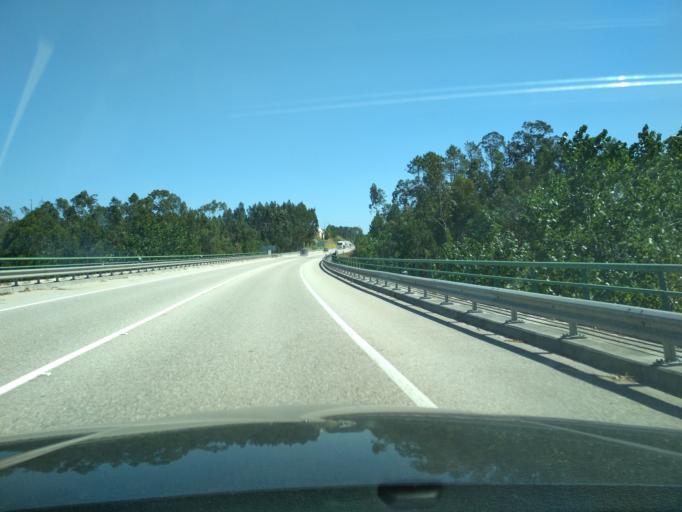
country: PT
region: Leiria
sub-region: Pombal
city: Lourical
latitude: 39.9877
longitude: -8.7365
